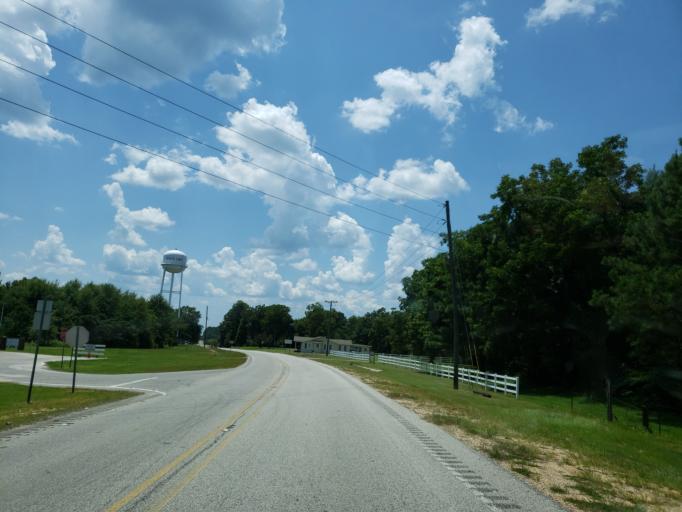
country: US
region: Mississippi
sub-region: Wayne County
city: Belmont
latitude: 31.4362
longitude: -88.4687
